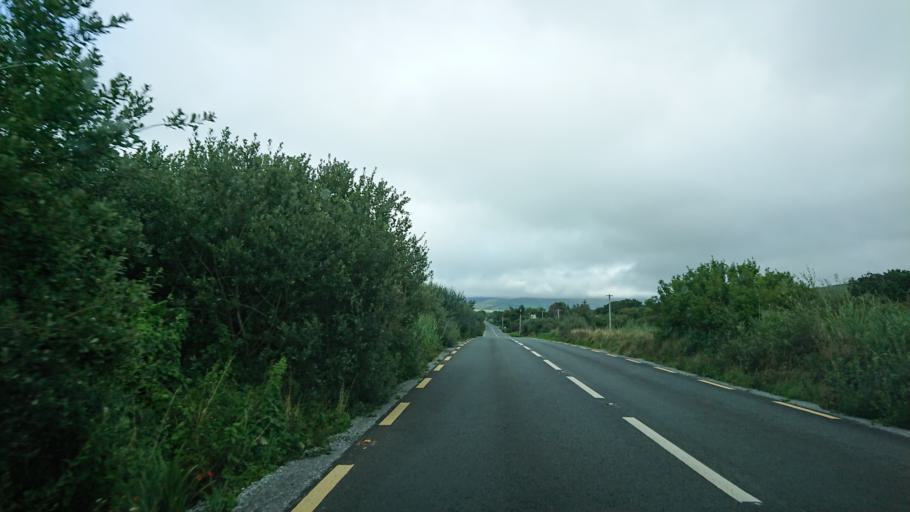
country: IE
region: Munster
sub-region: Ciarrai
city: Cahersiveen
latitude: 51.9593
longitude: -10.1873
